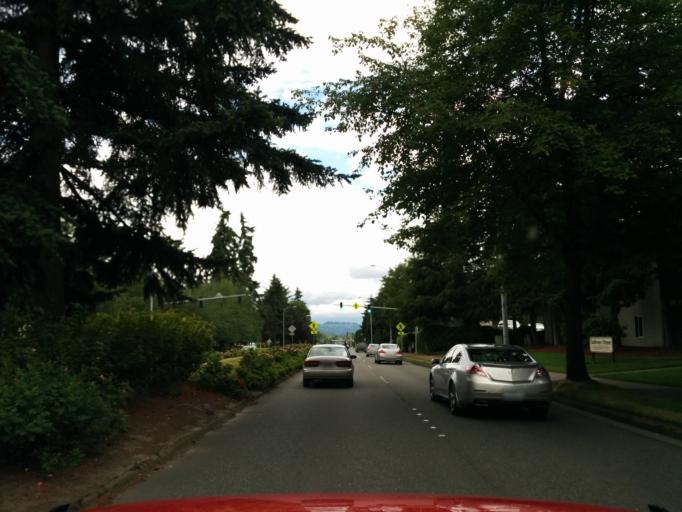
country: US
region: Washington
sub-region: King County
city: Redmond
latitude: 47.6400
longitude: -122.1431
